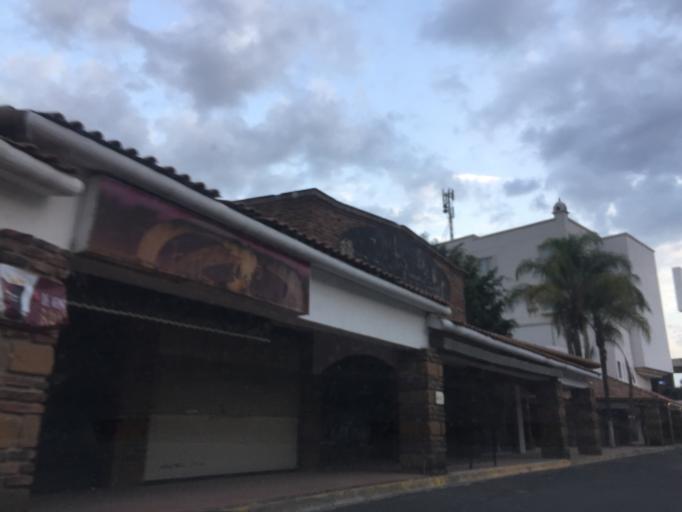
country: MX
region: Guanajuato
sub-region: Leon
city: La Ermita
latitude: 21.1697
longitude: -101.6923
